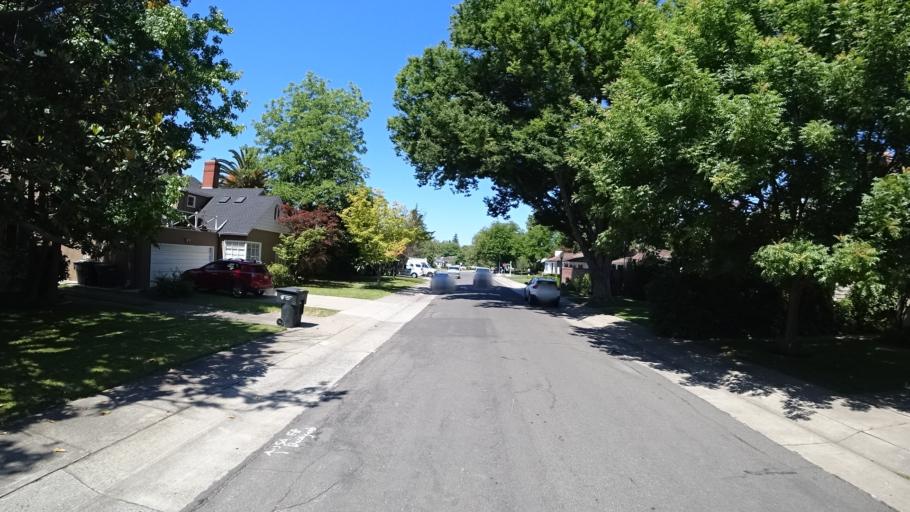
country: US
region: California
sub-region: Sacramento County
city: Sacramento
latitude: 38.5477
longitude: -121.4986
